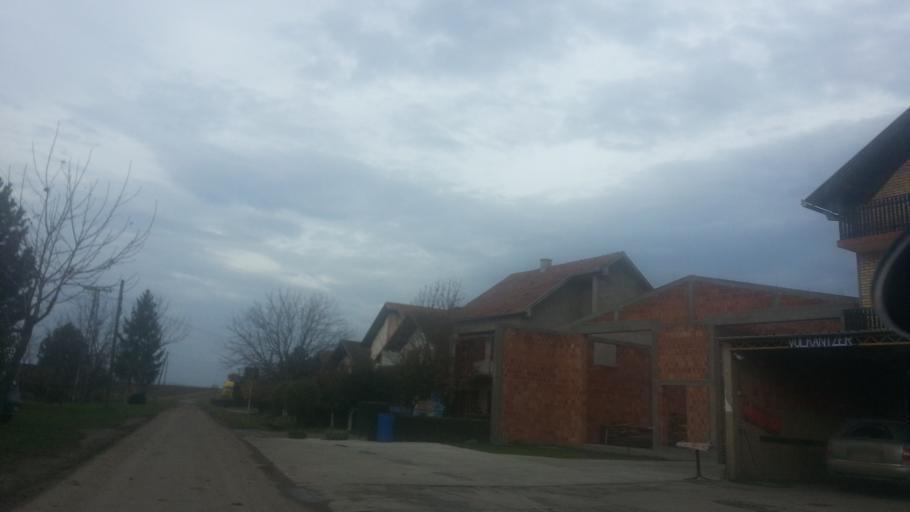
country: RS
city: Putinci
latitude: 44.9980
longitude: 19.9780
